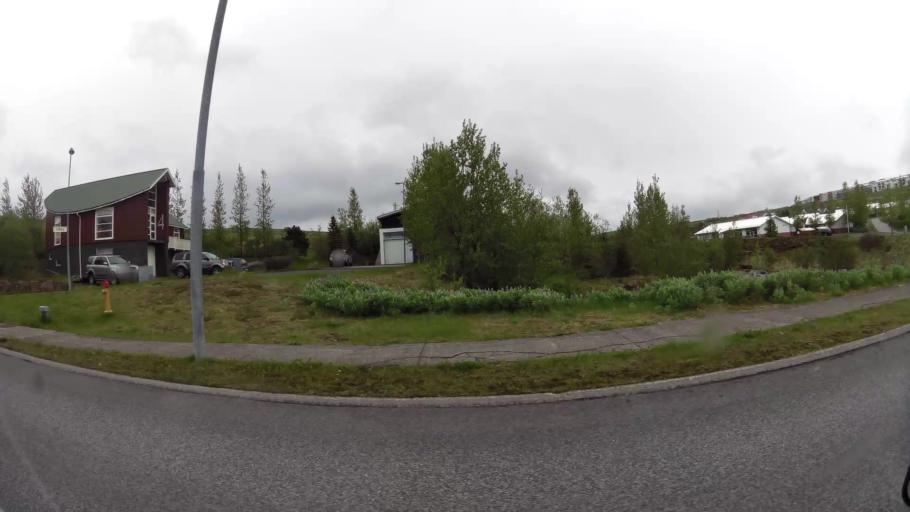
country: IS
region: Capital Region
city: Hafnarfjoerdur
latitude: 64.0587
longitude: -21.9255
